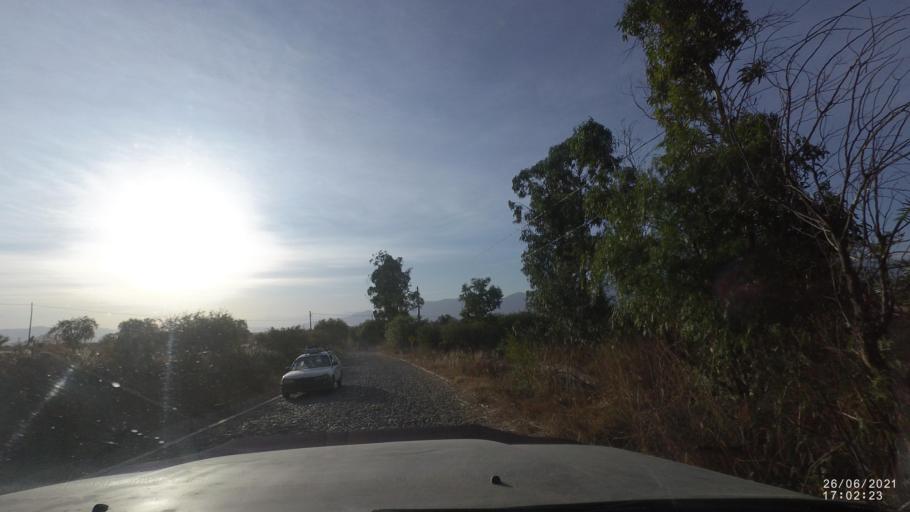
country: BO
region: Cochabamba
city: Cliza
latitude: -17.6539
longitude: -65.9125
